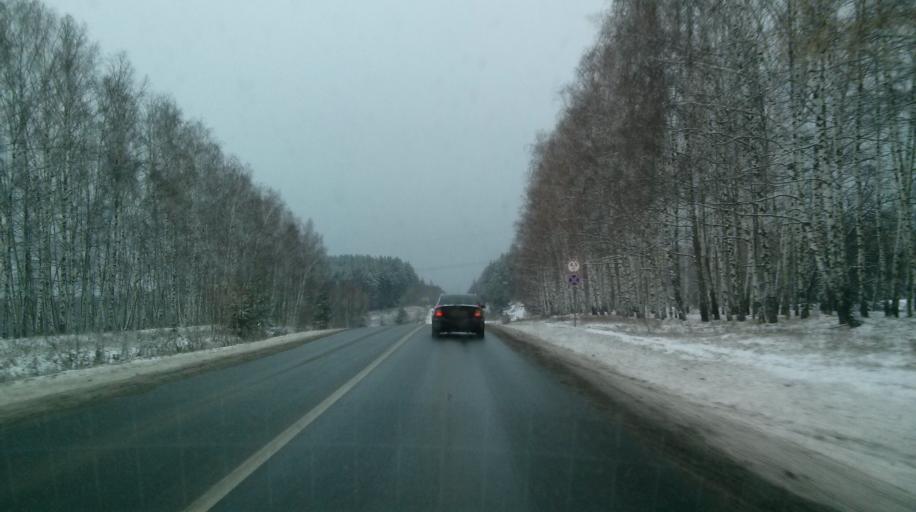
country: RU
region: Nizjnij Novgorod
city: Vorsma
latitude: 56.0270
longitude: 43.3582
